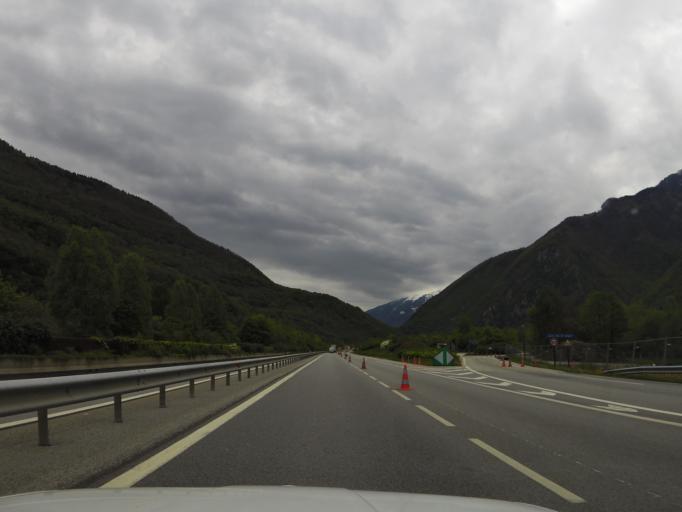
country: FR
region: Rhone-Alpes
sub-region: Departement de la Savoie
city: Saint-Remy-de-Maurienne
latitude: 45.4429
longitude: 6.2844
